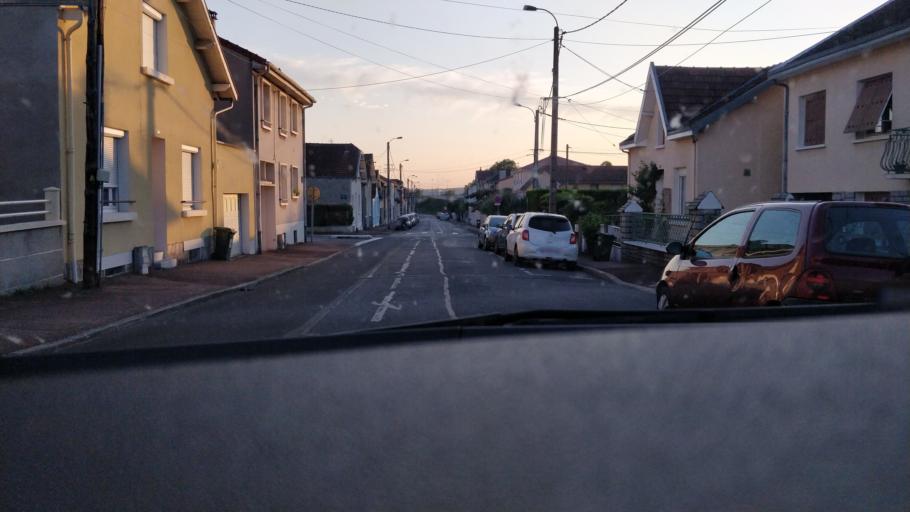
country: FR
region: Limousin
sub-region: Departement de la Haute-Vienne
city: Limoges
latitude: 45.8413
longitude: 1.2398
